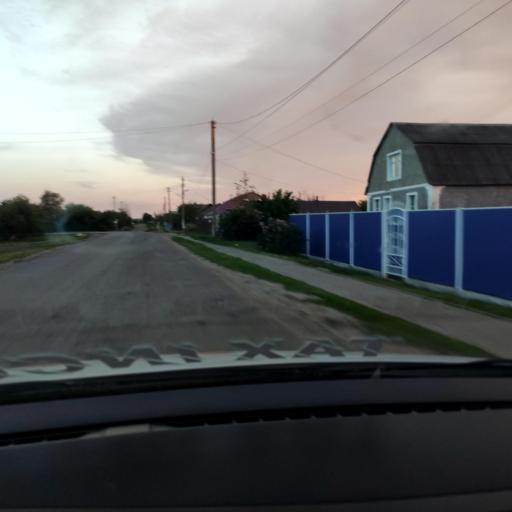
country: RU
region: Voronezj
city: Maslovka
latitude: 51.4534
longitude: 39.2403
